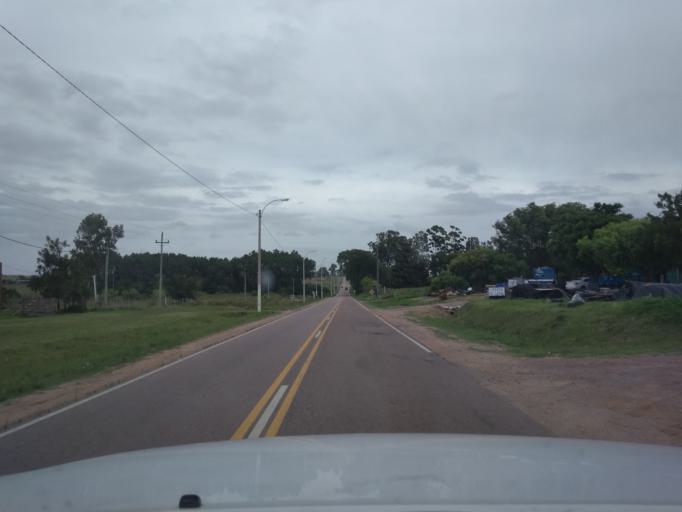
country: UY
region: Canelones
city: Tala
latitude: -34.3530
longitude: -55.7694
